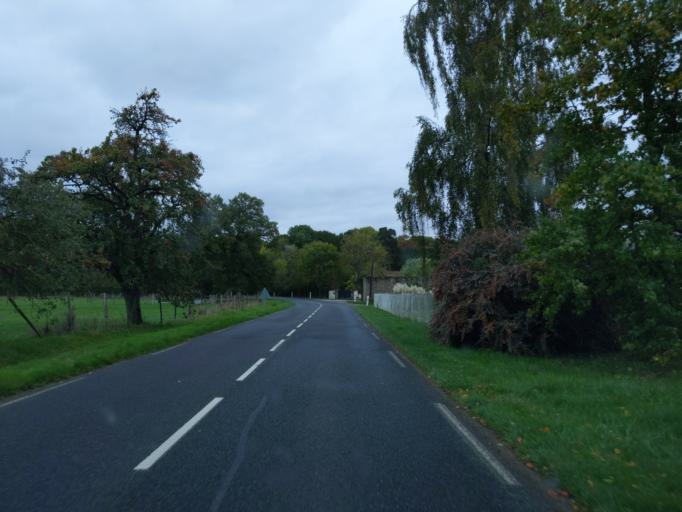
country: FR
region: Ile-de-France
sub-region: Departement des Yvelines
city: Bullion
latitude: 48.6400
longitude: 1.9877
